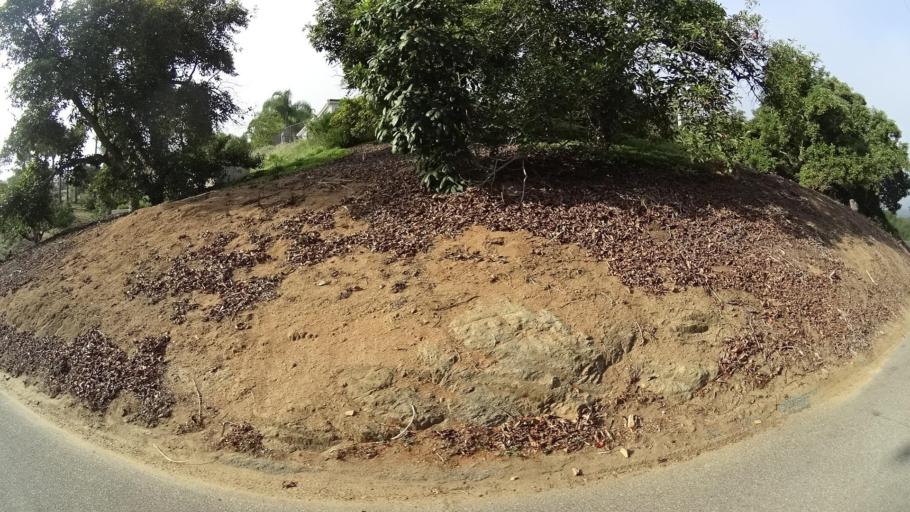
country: US
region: California
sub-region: San Diego County
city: Rainbow
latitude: 33.3397
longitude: -117.1688
